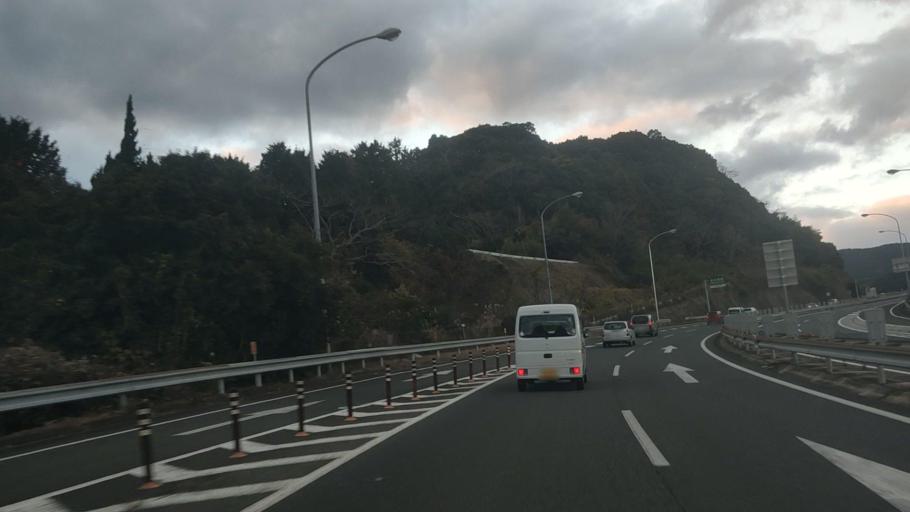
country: JP
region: Nagasaki
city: Obita
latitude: 32.8129
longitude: 129.9570
